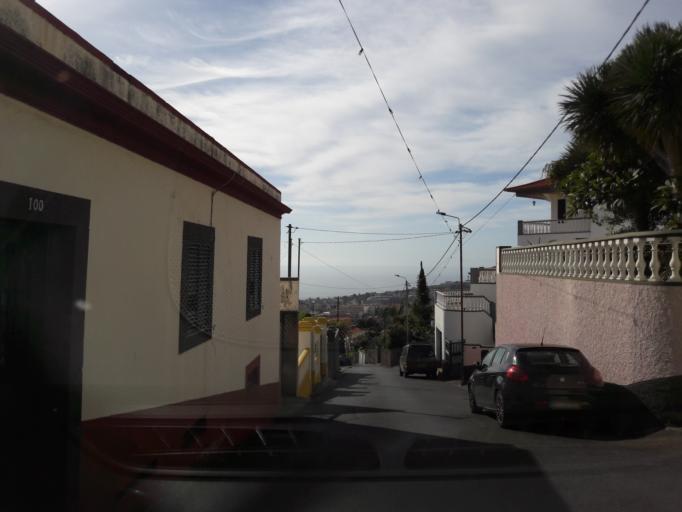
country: PT
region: Madeira
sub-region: Funchal
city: Nossa Senhora do Monte
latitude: 32.6663
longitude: -16.9226
